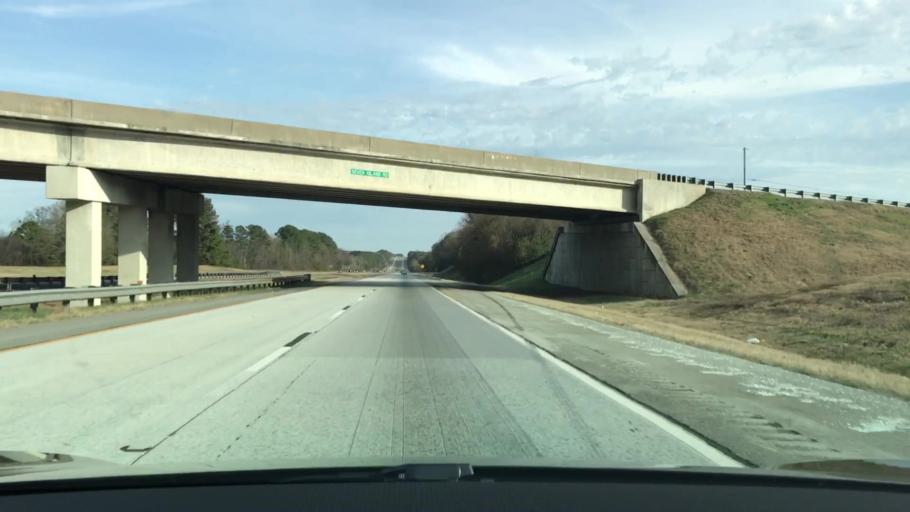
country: US
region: Georgia
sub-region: Putnam County
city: Jefferson
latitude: 33.5513
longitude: -83.3582
